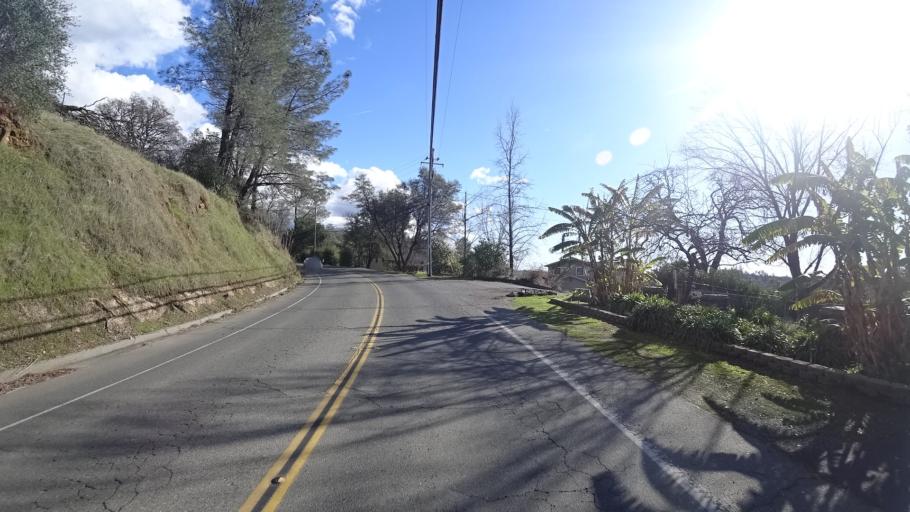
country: US
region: California
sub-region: Butte County
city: Oroville East
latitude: 39.5085
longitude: -121.5122
